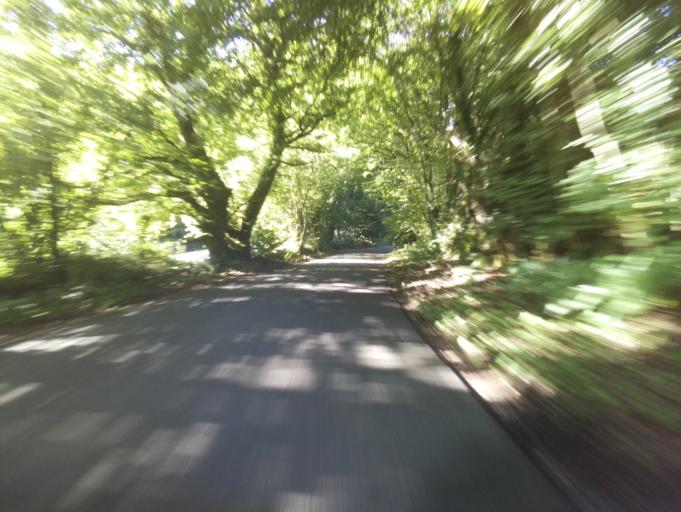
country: GB
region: Wales
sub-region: Monmouthshire
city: Tintern
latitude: 51.7194
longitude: -2.6904
